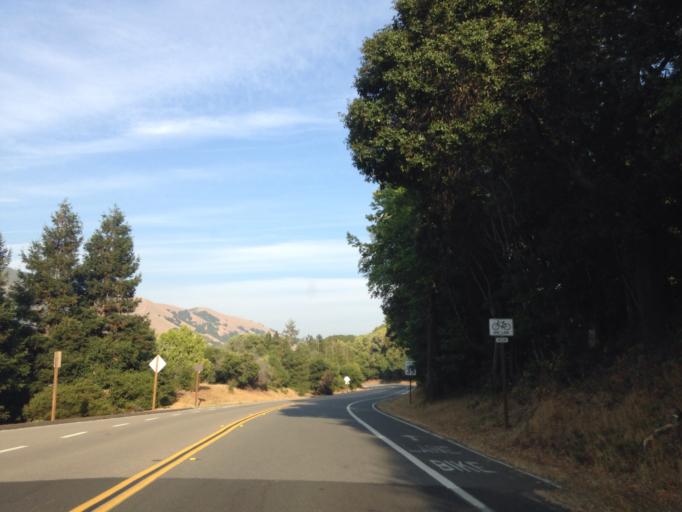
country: US
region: California
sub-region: Marin County
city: Lucas Valley-Marinwood
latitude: 38.0367
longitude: -122.5970
